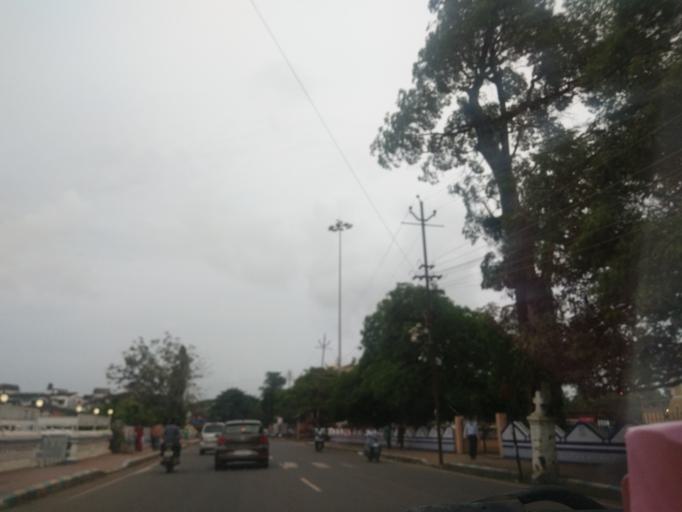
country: IN
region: Goa
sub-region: South Goa
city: Madgaon
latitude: 15.2572
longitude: 73.9662
